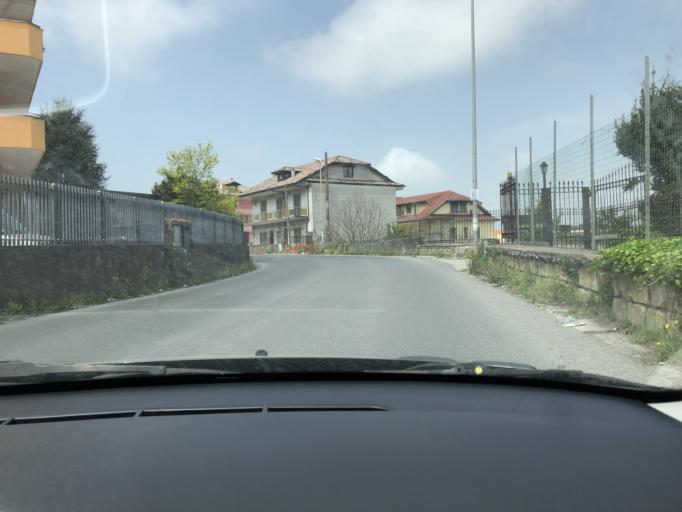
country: IT
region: Campania
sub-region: Provincia di Napoli
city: Torre Caracciolo
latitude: 40.8751
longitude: 14.1843
